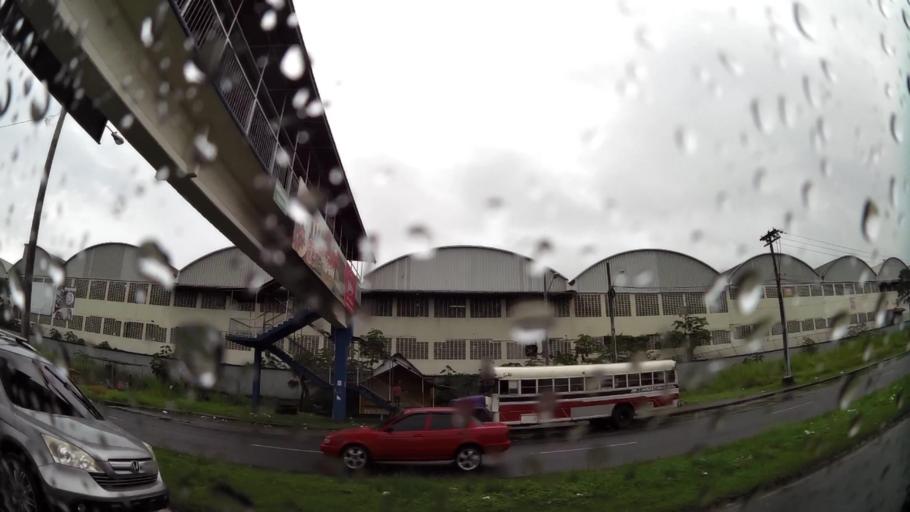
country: PA
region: Colon
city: Arco Iris
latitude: 9.3411
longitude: -79.8720
